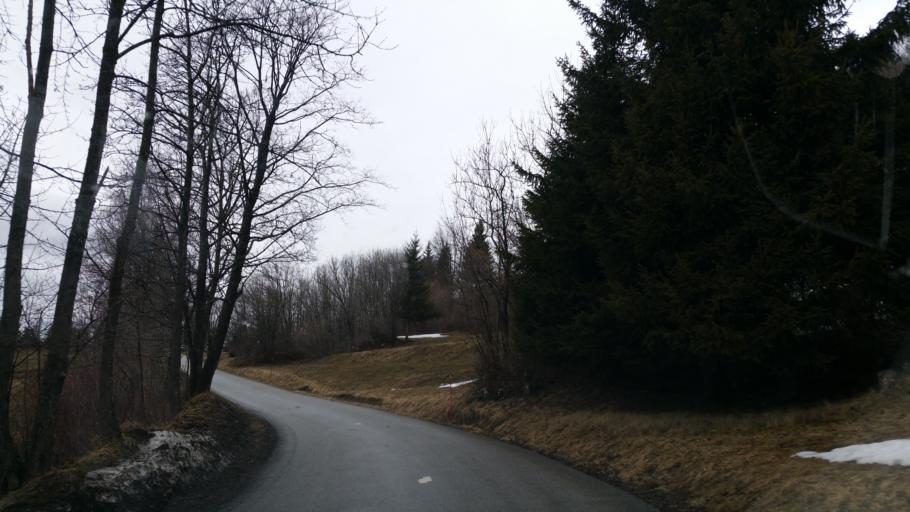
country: FR
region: Rhone-Alpes
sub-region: Departement de la Savoie
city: Villargondran
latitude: 45.2812
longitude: 6.3842
